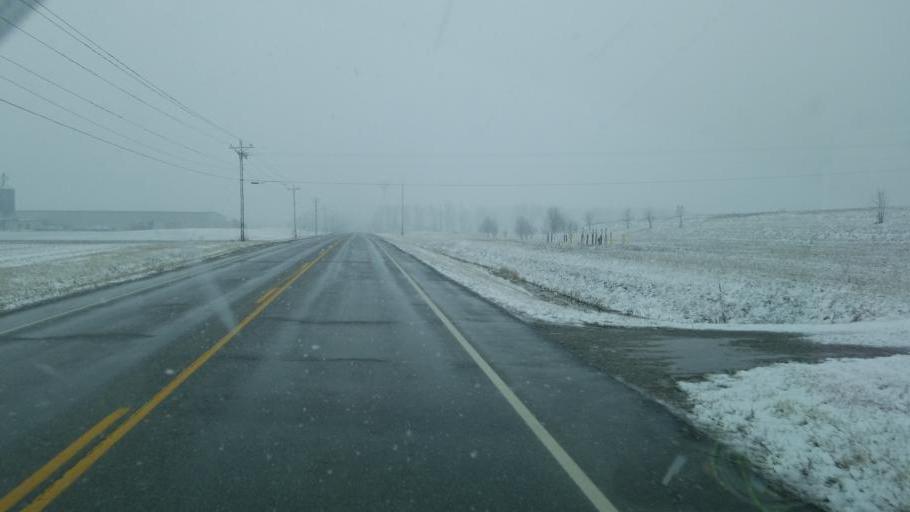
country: US
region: Ohio
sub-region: Champaign County
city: North Lewisburg
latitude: 40.2893
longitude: -83.5030
